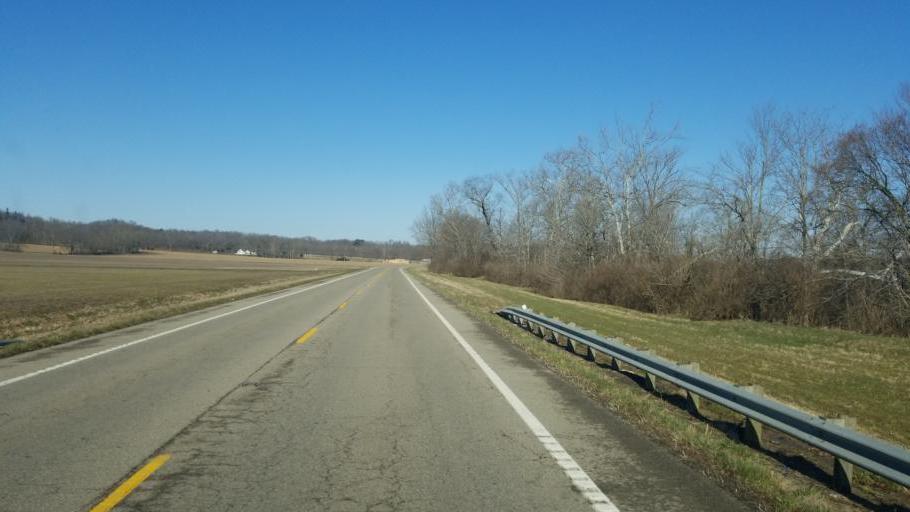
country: US
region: Ohio
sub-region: Highland County
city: Greenfield
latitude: 39.2223
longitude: -83.3059
